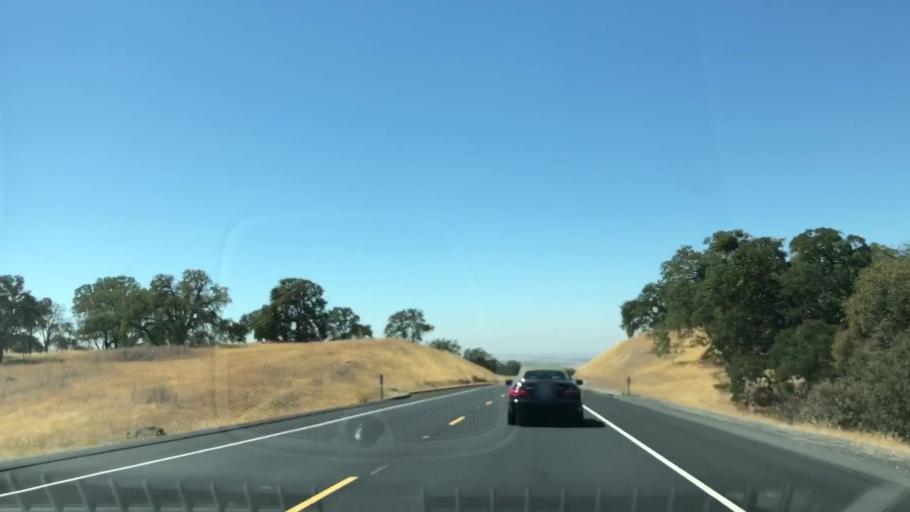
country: US
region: California
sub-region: Calaveras County
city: Copperopolis
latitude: 37.9422
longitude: -120.7369
